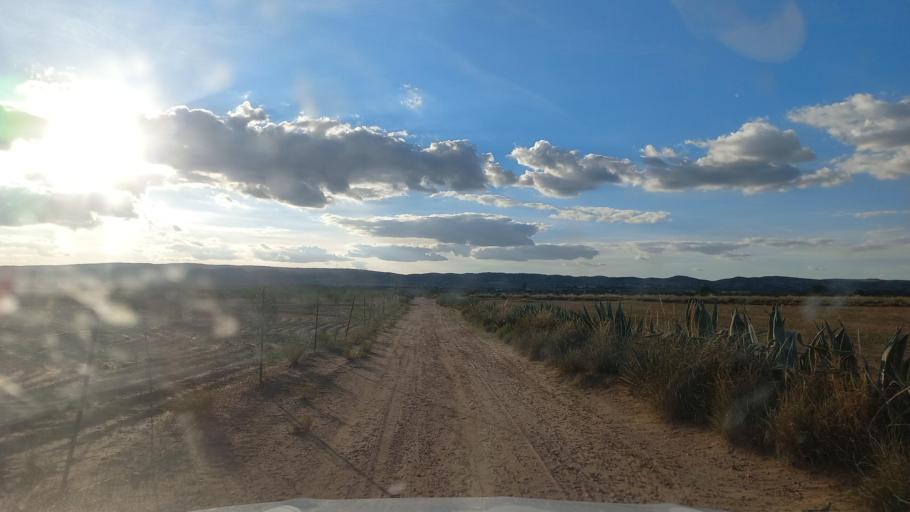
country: TN
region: Al Qasrayn
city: Sbiba
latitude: 35.3512
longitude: 9.0378
